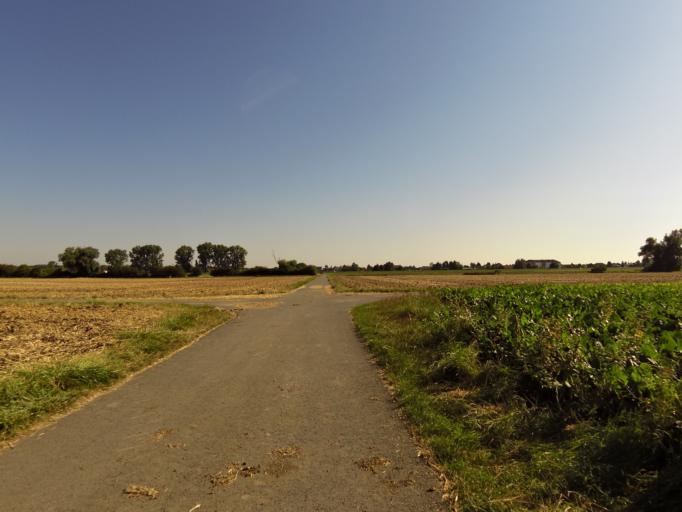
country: DE
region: Hesse
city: Biebesheim
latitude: 49.7962
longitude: 8.4547
